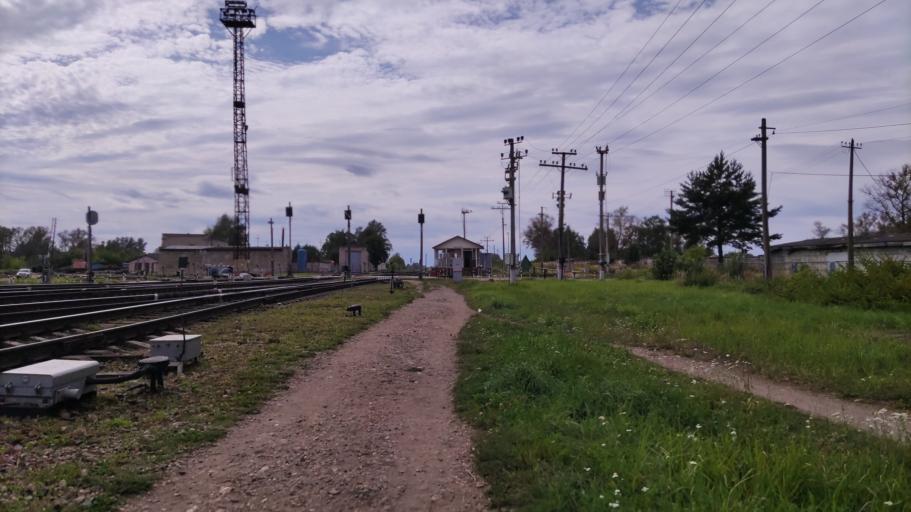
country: RU
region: Tverskaya
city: Rzhev
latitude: 56.2393
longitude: 34.3147
